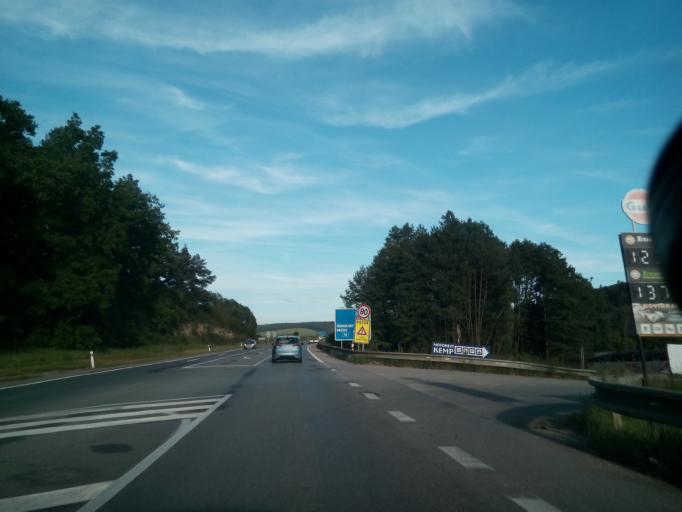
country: SK
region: Presovsky
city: Sabinov
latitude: 49.0039
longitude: 21.0995
